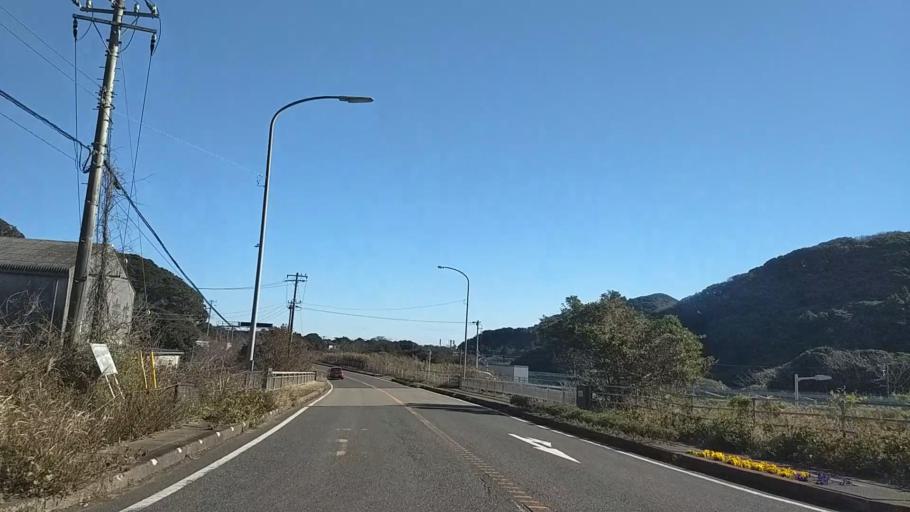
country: JP
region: Chiba
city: Kawaguchi
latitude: 35.1232
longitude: 140.1439
